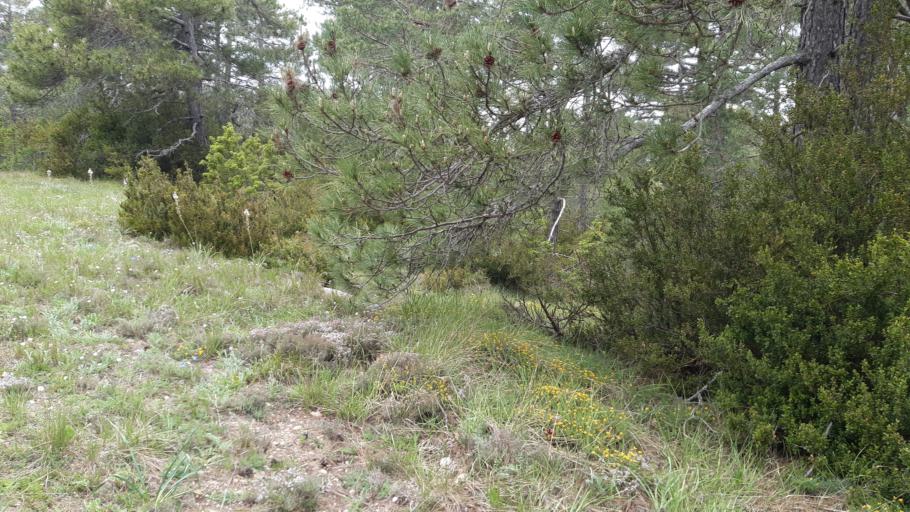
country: ES
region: Aragon
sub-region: Provincia de Teruel
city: Valderrobres
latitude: 40.7803
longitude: 0.2363
